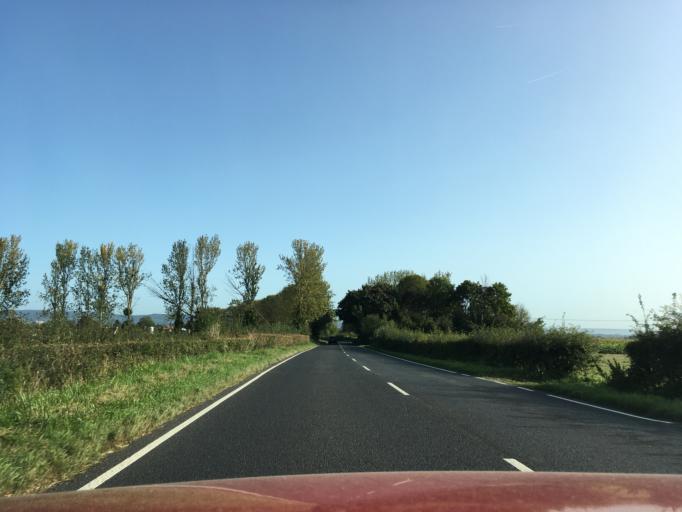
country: GB
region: England
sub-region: Gloucestershire
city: Gloucester
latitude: 51.8939
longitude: -2.2813
